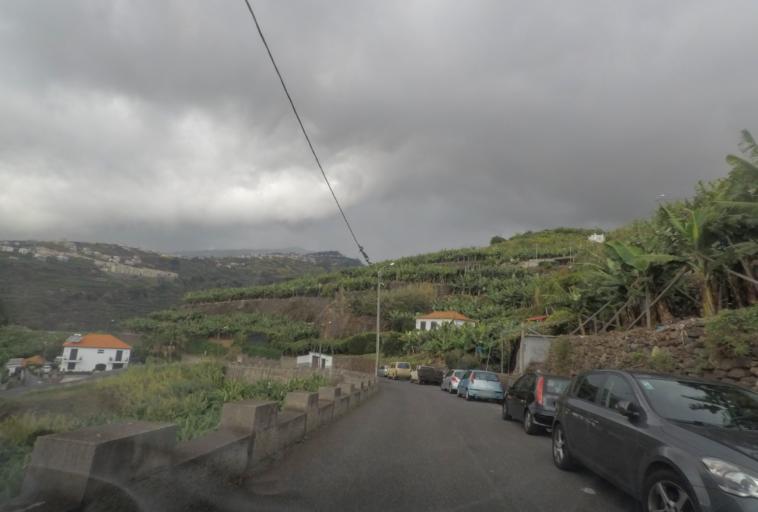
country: PT
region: Madeira
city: Camara de Lobos
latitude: 32.6597
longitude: -16.9563
